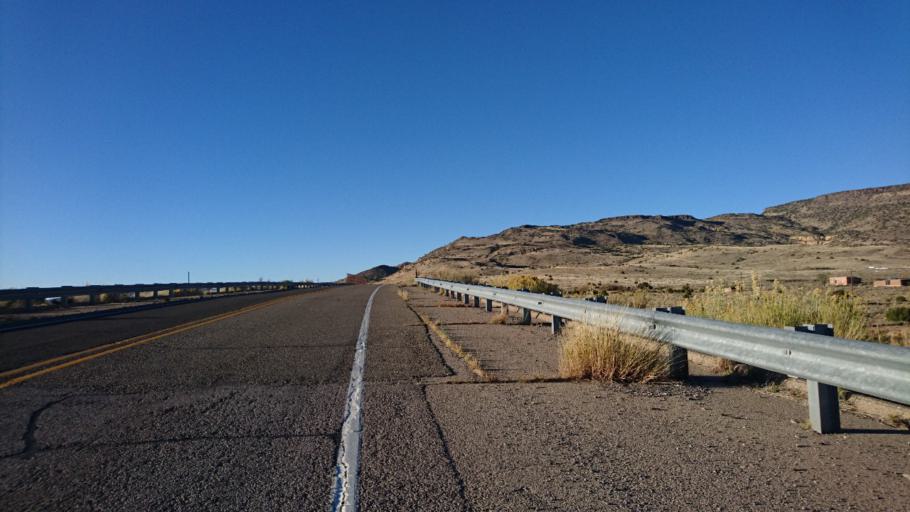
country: US
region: New Mexico
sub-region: Cibola County
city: Grants
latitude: 35.1055
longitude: -107.7796
